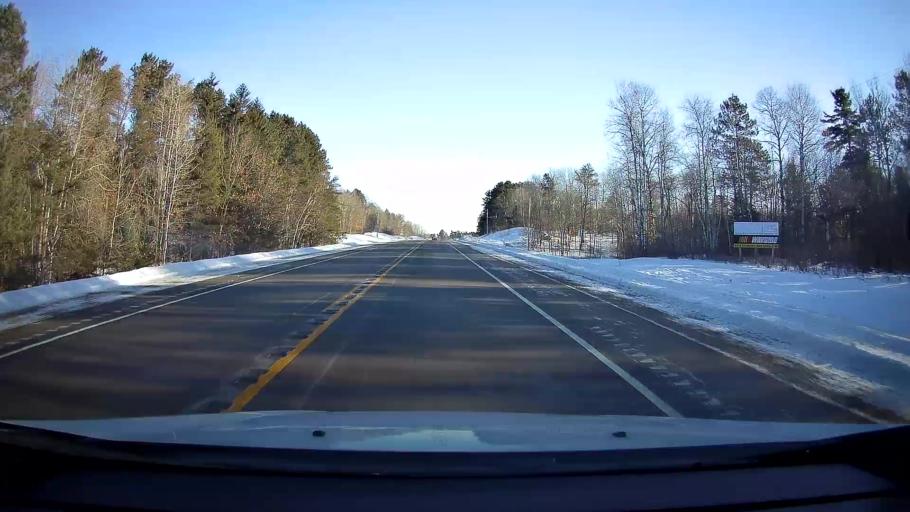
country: US
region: Wisconsin
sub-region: Sawyer County
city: Hayward
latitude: 46.0704
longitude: -91.4297
